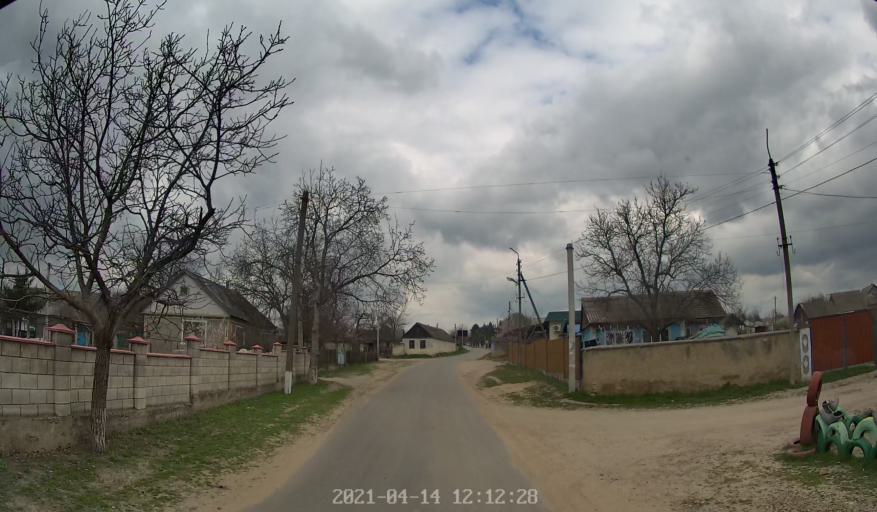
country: MD
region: Criuleni
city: Criuleni
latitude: 47.1667
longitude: 29.1980
